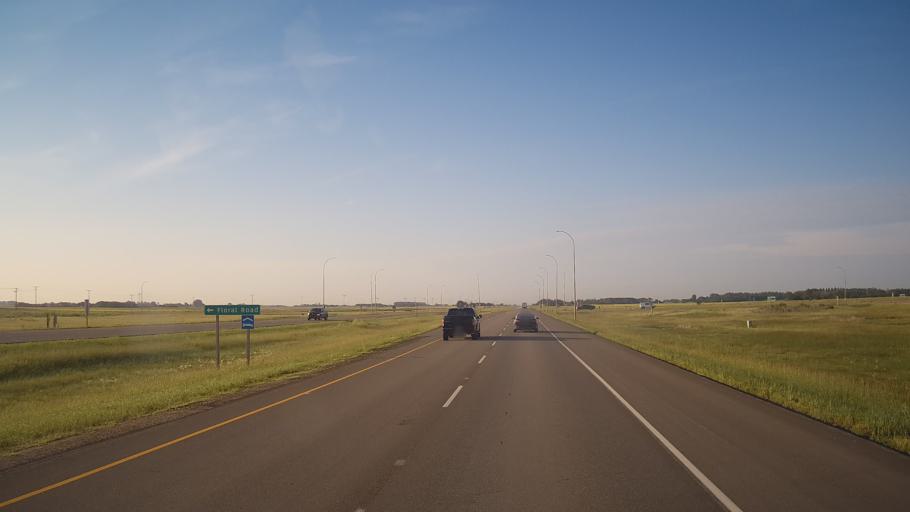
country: CA
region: Saskatchewan
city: Saskatoon
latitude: 52.0562
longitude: -106.5993
